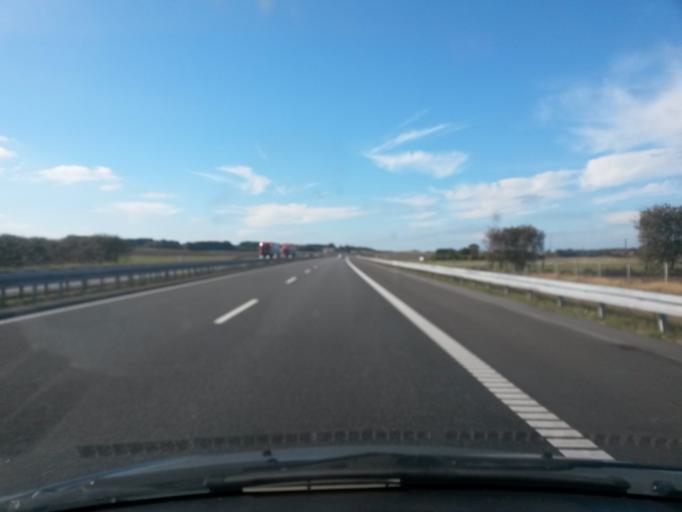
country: DK
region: Central Jutland
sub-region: Silkeborg Kommune
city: Svejbaek
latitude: 56.1479
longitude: 9.6666
